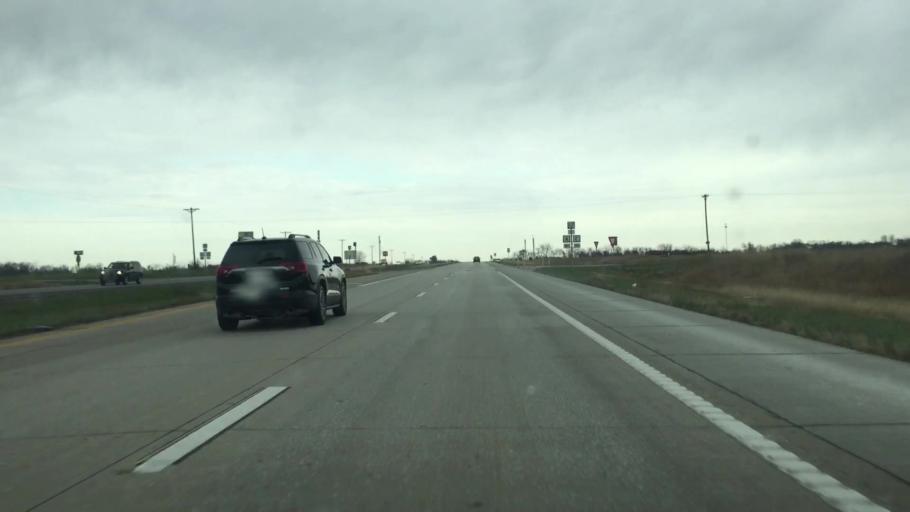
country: US
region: Missouri
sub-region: Saint Clair County
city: Osceola
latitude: 38.1507
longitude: -93.7227
